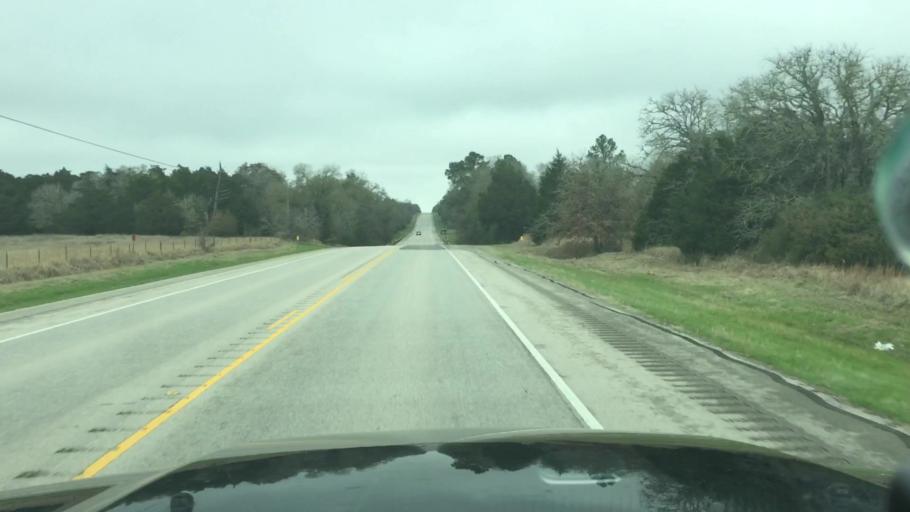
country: US
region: Texas
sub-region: Lee County
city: Giddings
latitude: 30.0661
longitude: -96.9164
